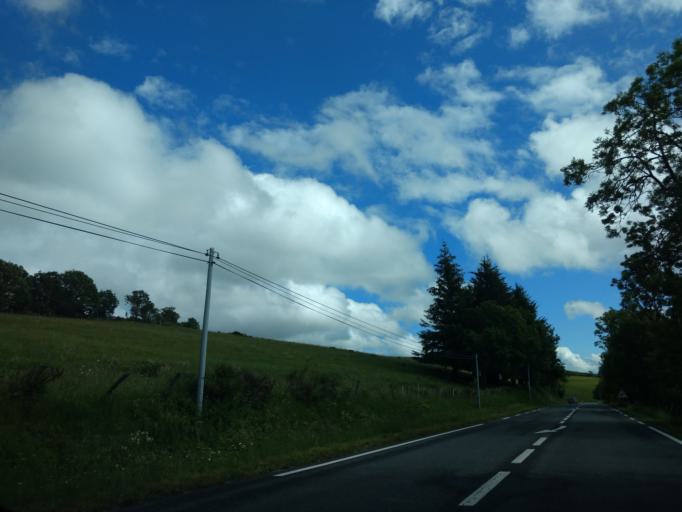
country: FR
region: Midi-Pyrenees
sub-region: Departement de l'Aveyron
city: Laguiole
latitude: 44.6721
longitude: 2.8500
